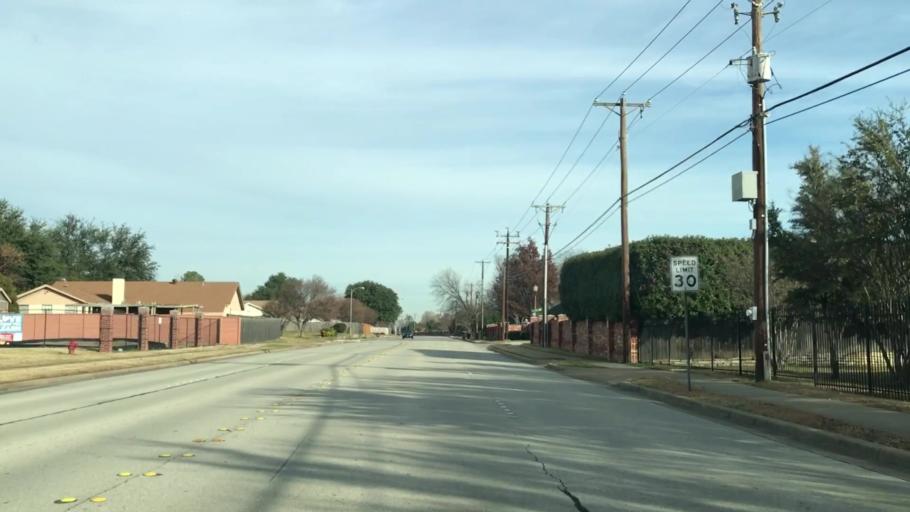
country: US
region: Texas
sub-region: Tarrant County
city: Watauga
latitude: 32.8832
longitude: -97.2118
